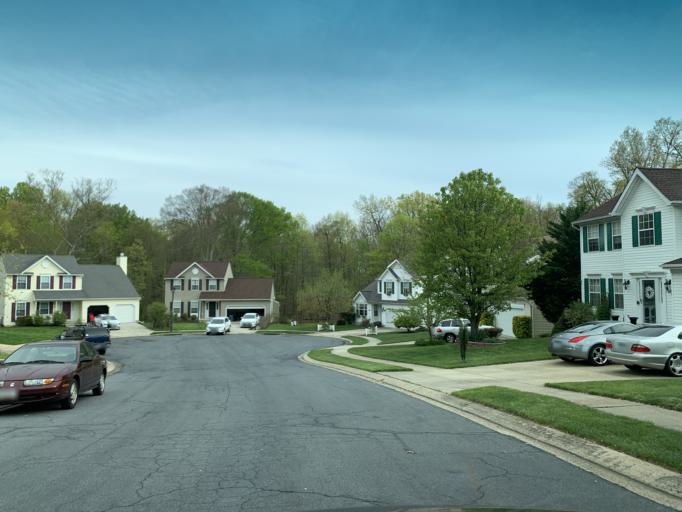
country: US
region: Maryland
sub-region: Harford County
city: Riverside
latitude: 39.4747
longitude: -76.2554
